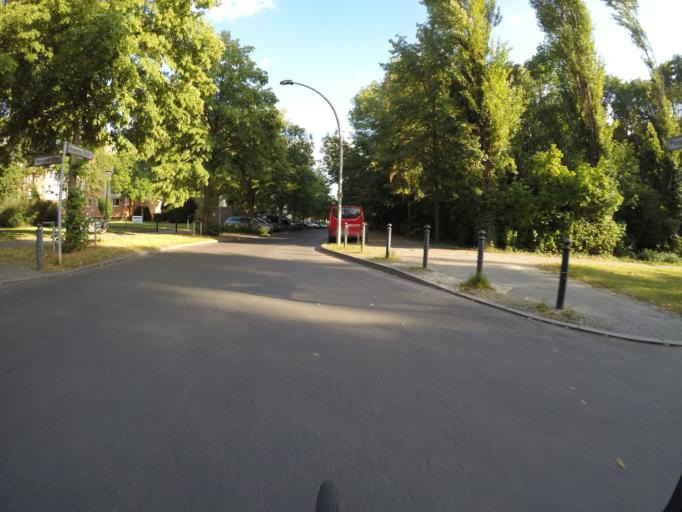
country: DE
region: Berlin
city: Weissensee
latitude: 52.5576
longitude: 13.4782
